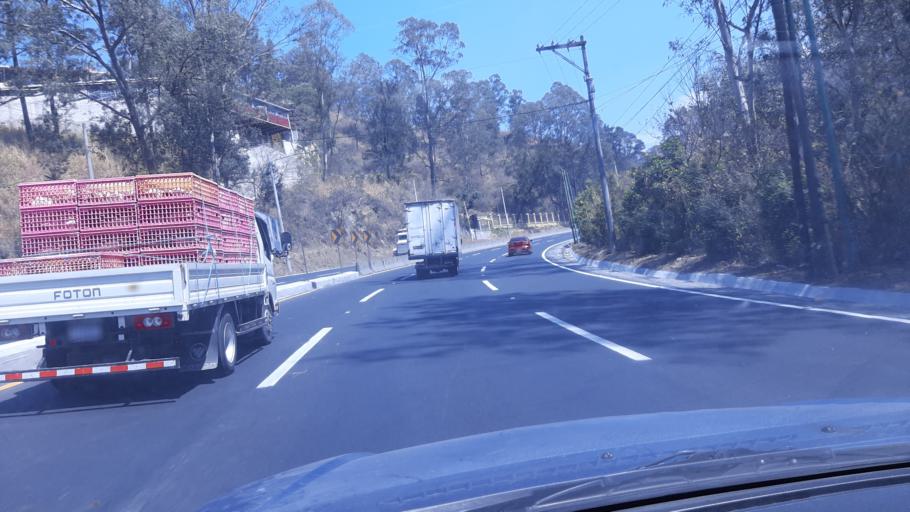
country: GT
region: Guatemala
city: Amatitlan
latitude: 14.4952
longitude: -90.6289
